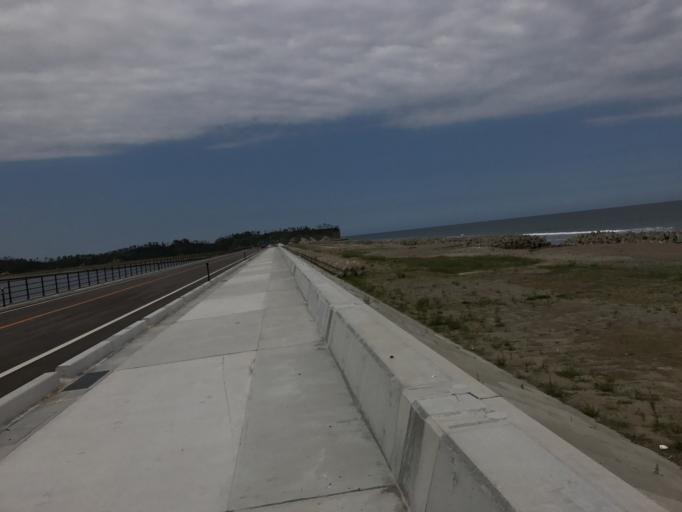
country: JP
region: Miyagi
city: Marumori
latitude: 37.8126
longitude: 140.9855
